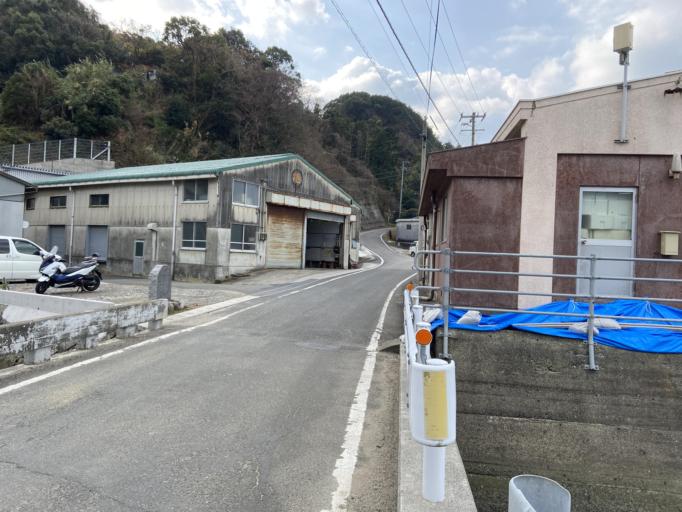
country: JP
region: Ehime
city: Uwajima
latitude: 33.2620
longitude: 132.5428
